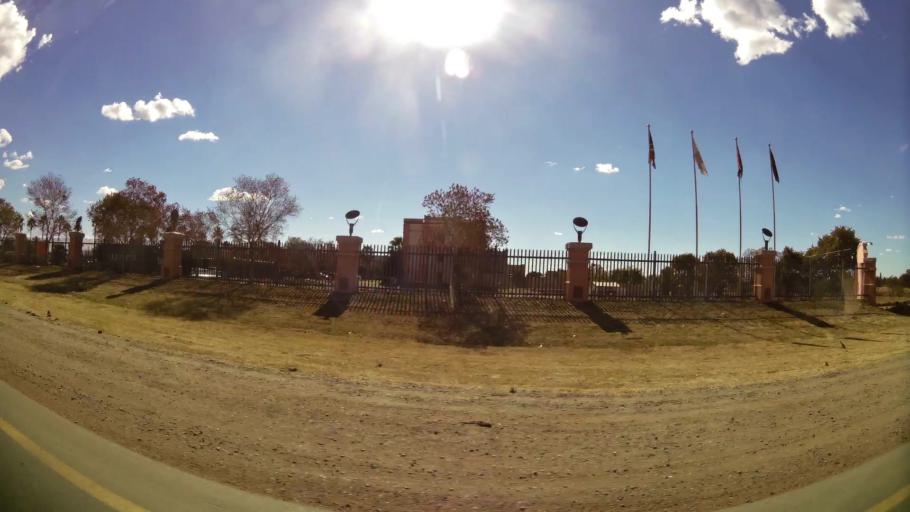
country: ZA
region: North-West
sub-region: Dr Kenneth Kaunda District Municipality
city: Klerksdorp
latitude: -26.8694
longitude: 26.6219
